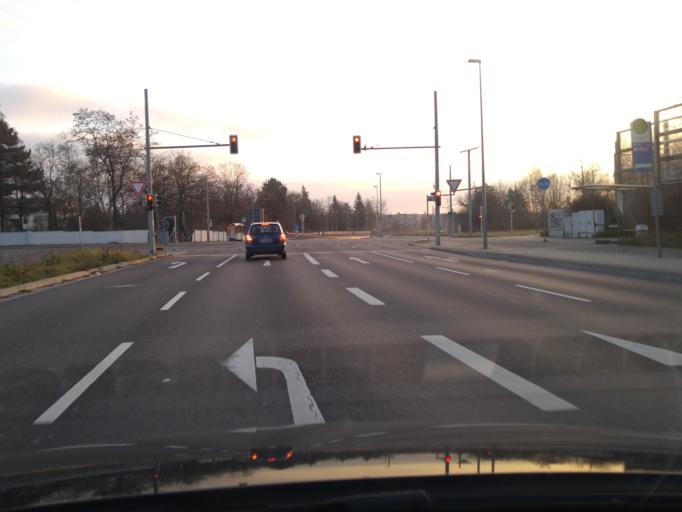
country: DE
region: Saxony
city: Leipzig
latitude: 51.3757
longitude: 12.3450
